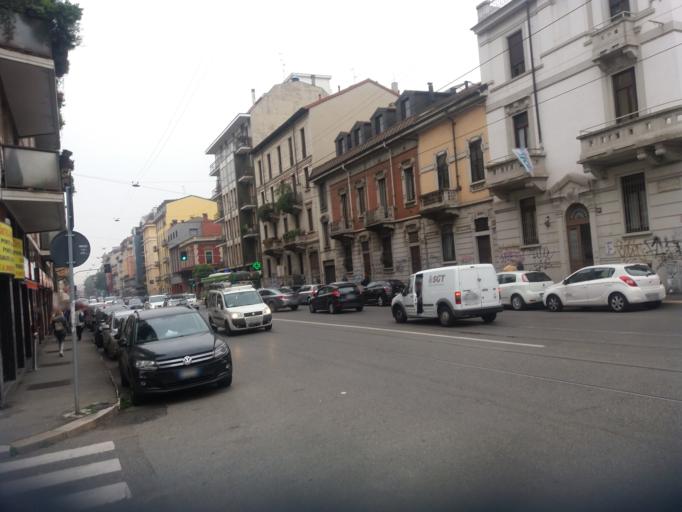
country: IT
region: Lombardy
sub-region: Citta metropolitana di Milano
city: Milano
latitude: 45.4861
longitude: 9.2253
